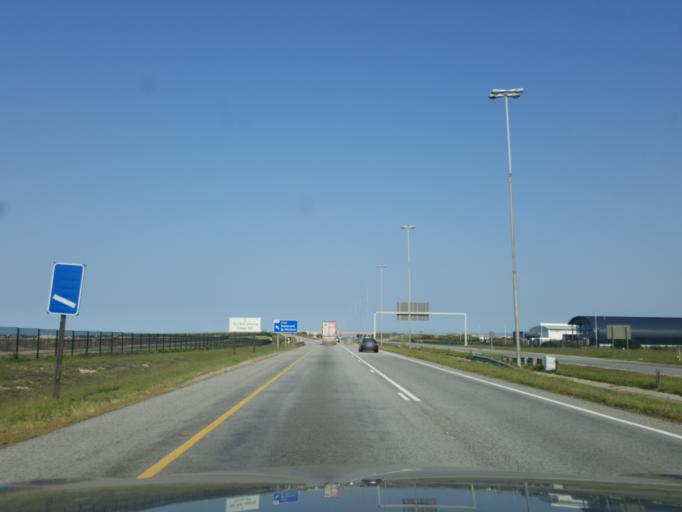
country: ZA
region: Eastern Cape
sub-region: Nelson Mandela Bay Metropolitan Municipality
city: Port Elizabeth
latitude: -33.8172
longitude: 25.6495
